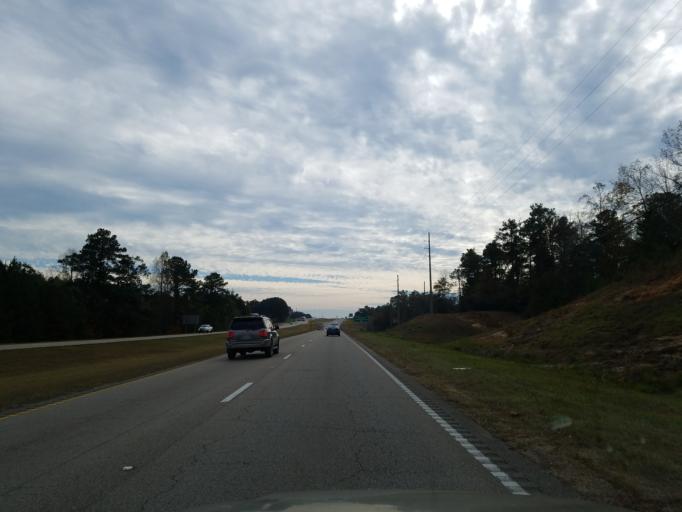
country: US
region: Mississippi
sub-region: Forrest County
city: Hattiesburg
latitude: 31.2543
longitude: -89.2799
